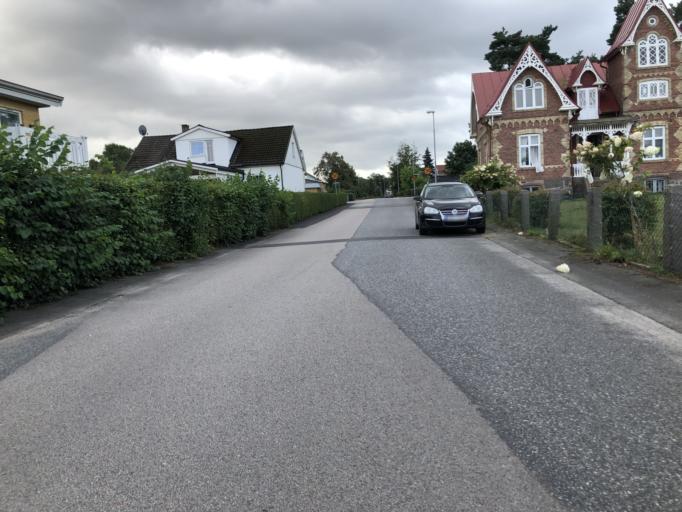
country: SE
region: Skane
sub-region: Hassleholms Kommun
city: Vinslov
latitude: 56.1029
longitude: 13.9170
